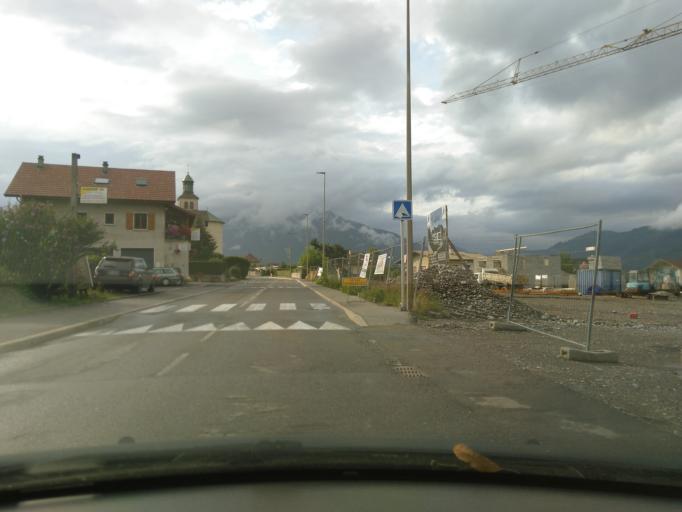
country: FR
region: Rhone-Alpes
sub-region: Departement de la Haute-Savoie
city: Marnaz
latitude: 46.0578
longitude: 6.5364
